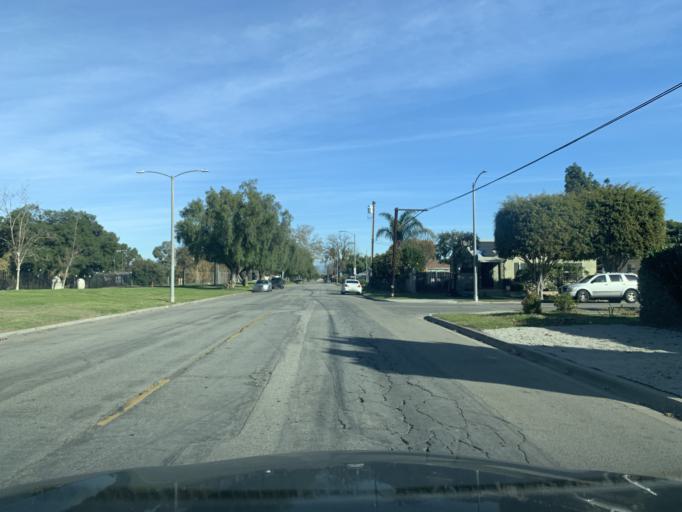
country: US
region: California
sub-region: Los Angeles County
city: East Rancho Dominguez
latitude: 33.8628
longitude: -118.1945
